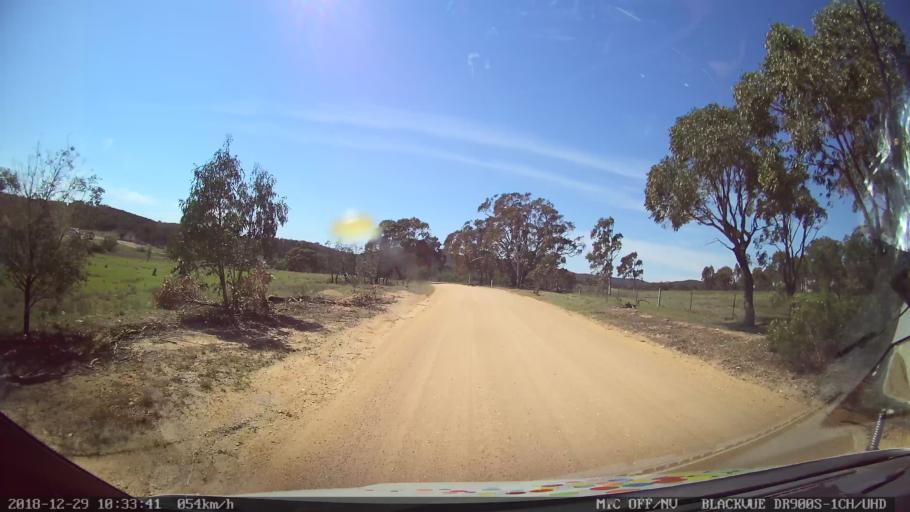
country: AU
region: New South Wales
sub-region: Yass Valley
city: Gundaroo
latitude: -34.9824
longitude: 149.4731
